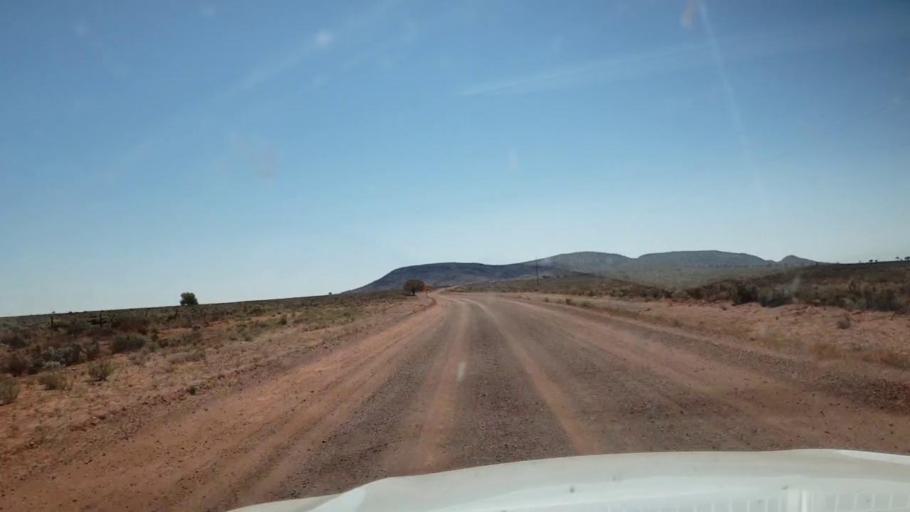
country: AU
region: South Australia
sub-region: Whyalla
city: Whyalla
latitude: -32.7113
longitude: 137.1408
